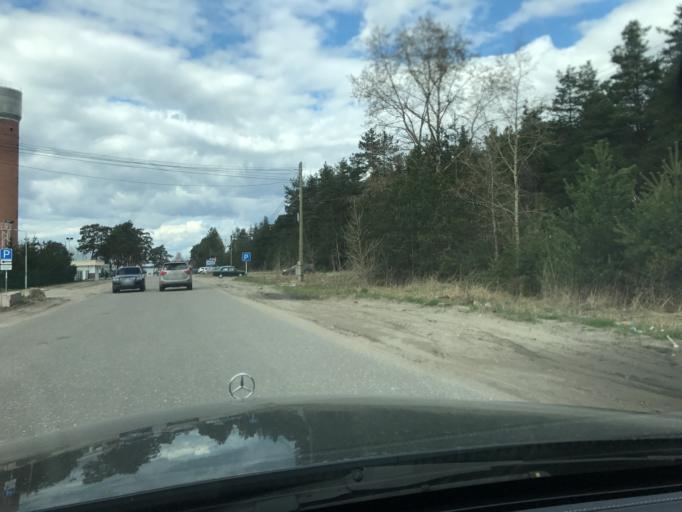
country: RU
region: Vladimir
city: Pokrov
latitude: 55.9016
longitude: 39.1957
